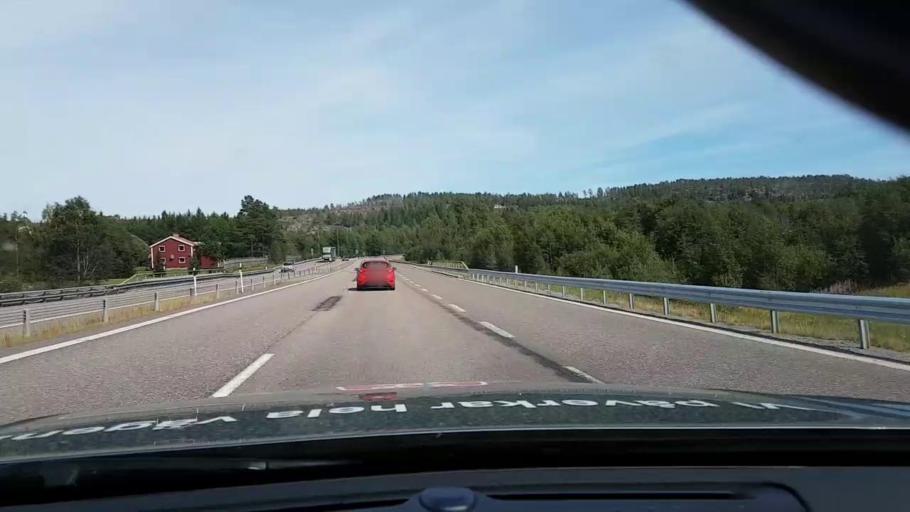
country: SE
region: Vaesternorrland
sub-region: OErnskoeldsviks Kommun
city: Ornskoldsvik
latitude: 63.3129
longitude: 18.7903
